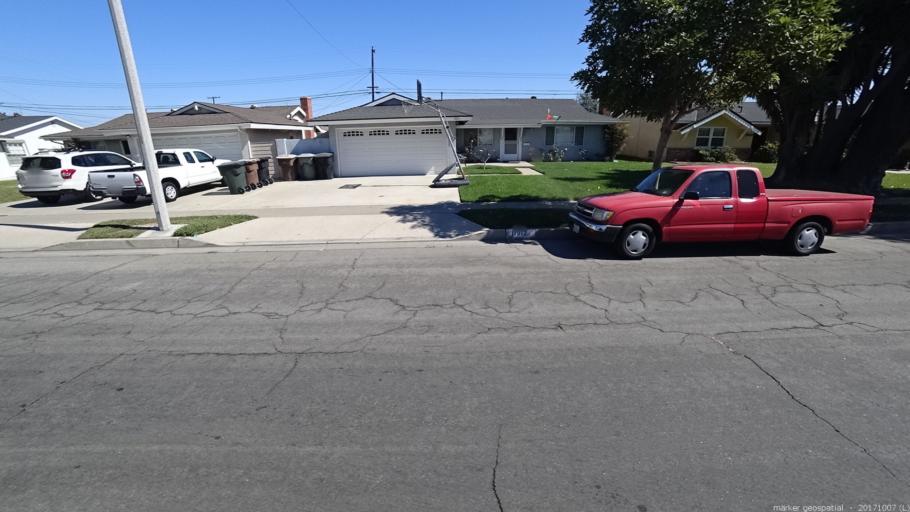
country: US
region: California
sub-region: Orange County
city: Cypress
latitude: 33.7912
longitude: -118.0355
